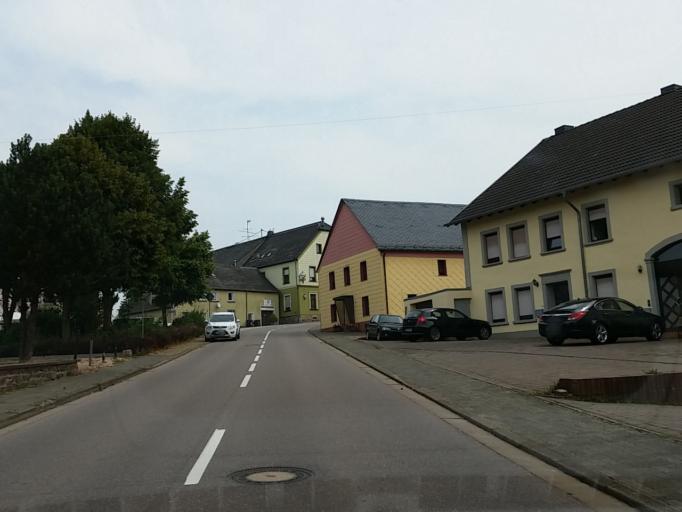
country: DE
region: Saarland
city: Nonnweiler
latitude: 49.5741
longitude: 6.9307
